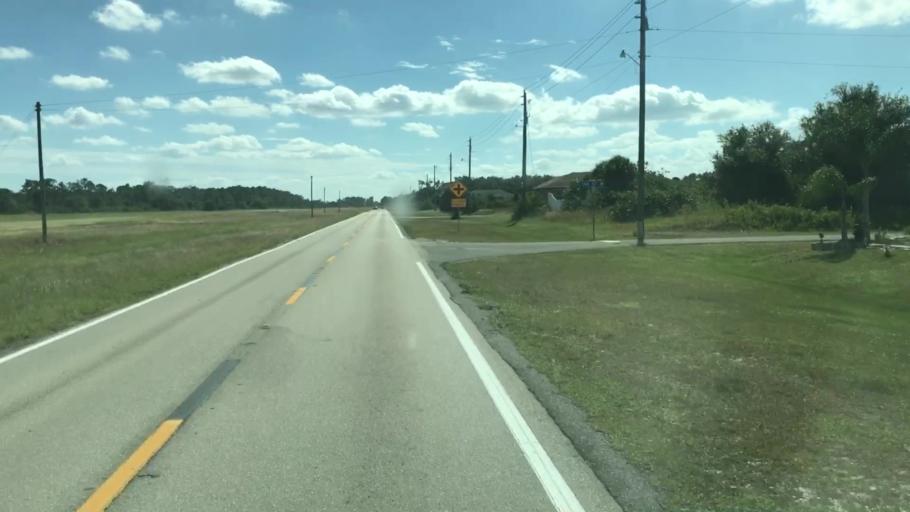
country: US
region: Florida
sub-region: Lee County
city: Lehigh Acres
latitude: 26.6551
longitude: -81.6636
